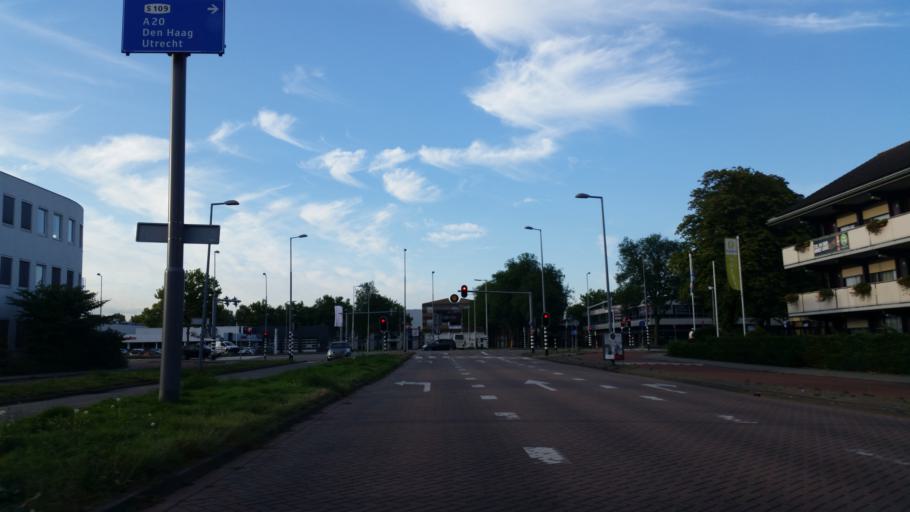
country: NL
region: South Holland
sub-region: Gemeente Rotterdam
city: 's-Gravenland
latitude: 51.9468
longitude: 4.5440
